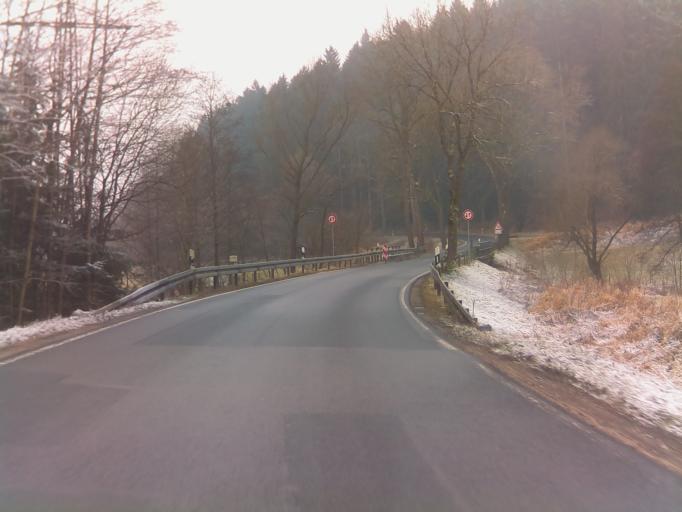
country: DE
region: Thuringia
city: Viernau
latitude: 50.6475
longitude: 10.5561
